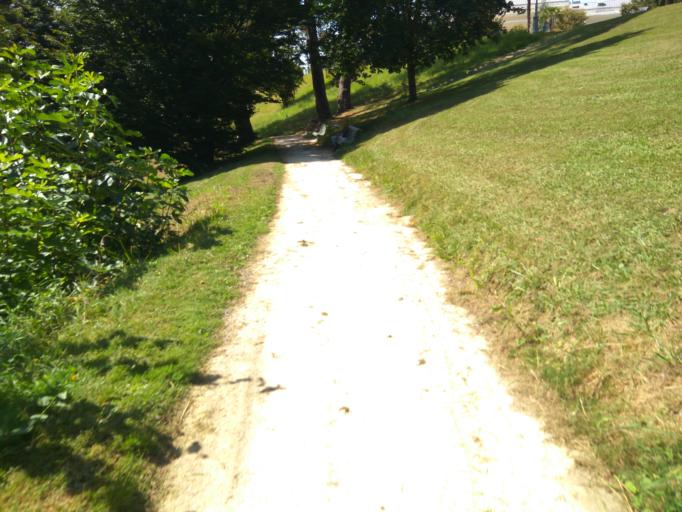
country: FR
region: Aquitaine
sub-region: Departement des Pyrenees-Atlantiques
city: Pau
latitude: 43.2951
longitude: -0.3598
